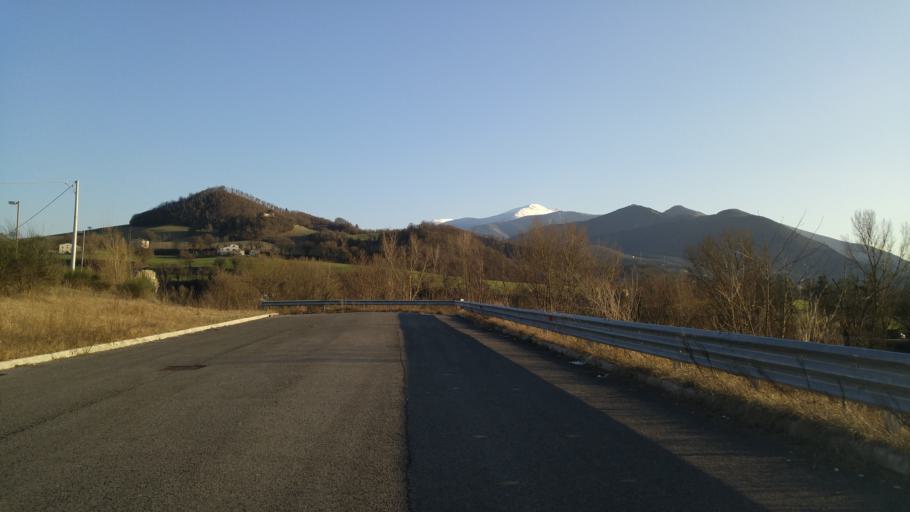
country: IT
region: The Marches
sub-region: Provincia di Pesaro e Urbino
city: Cagli
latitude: 43.5616
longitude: 12.6573
